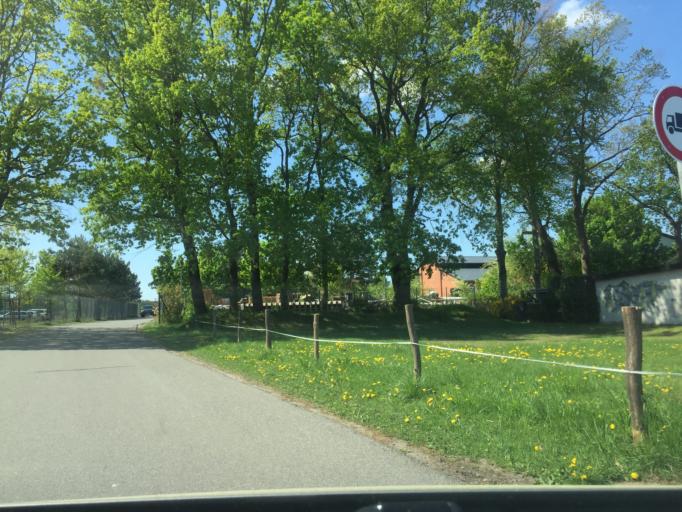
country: DE
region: Mecklenburg-Vorpommern
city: Torgelow
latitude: 53.6349
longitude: 14.0325
